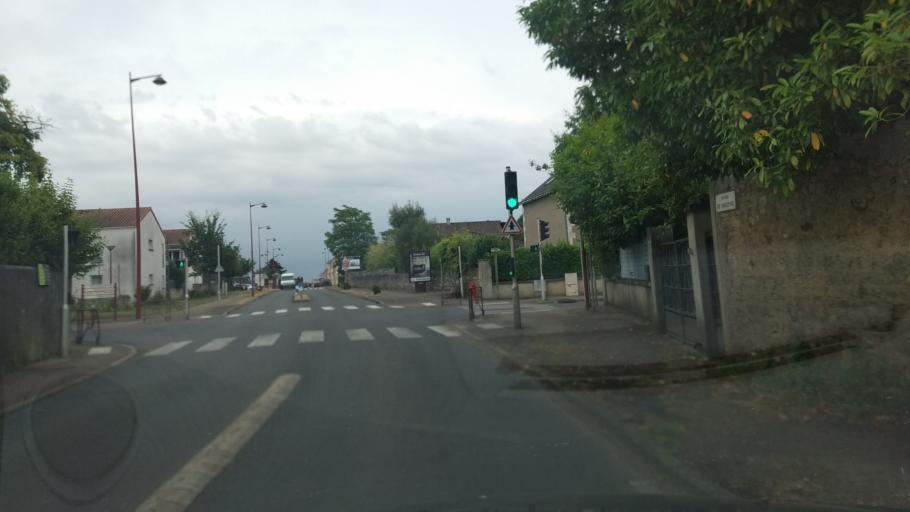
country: FR
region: Poitou-Charentes
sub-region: Departement de la Vienne
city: Biard
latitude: 46.5762
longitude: 0.3053
